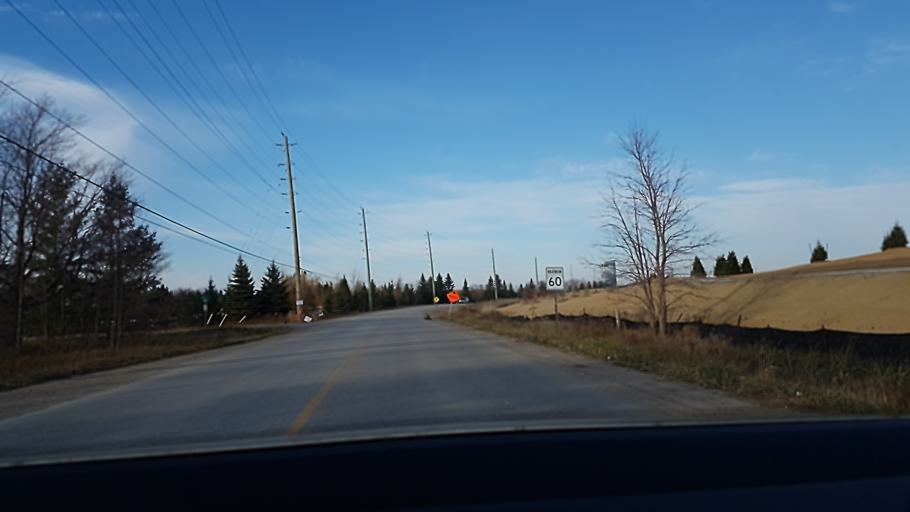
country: CA
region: Ontario
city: Barrie
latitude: 44.3835
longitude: -79.5550
